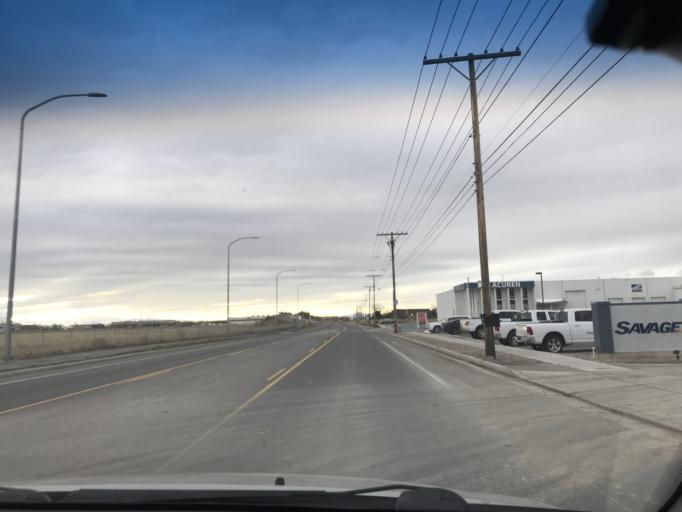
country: US
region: Utah
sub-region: Davis County
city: North Salt Lake
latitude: 40.8420
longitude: -111.9363
